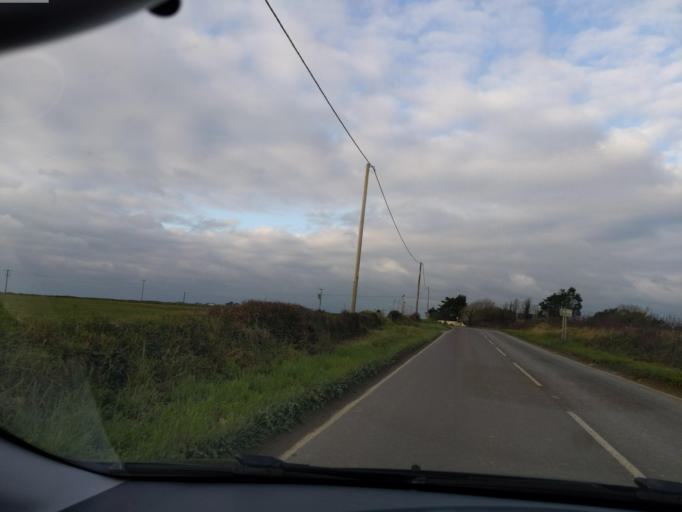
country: GB
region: England
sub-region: Cornwall
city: Padstow
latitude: 50.5229
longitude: -4.9521
